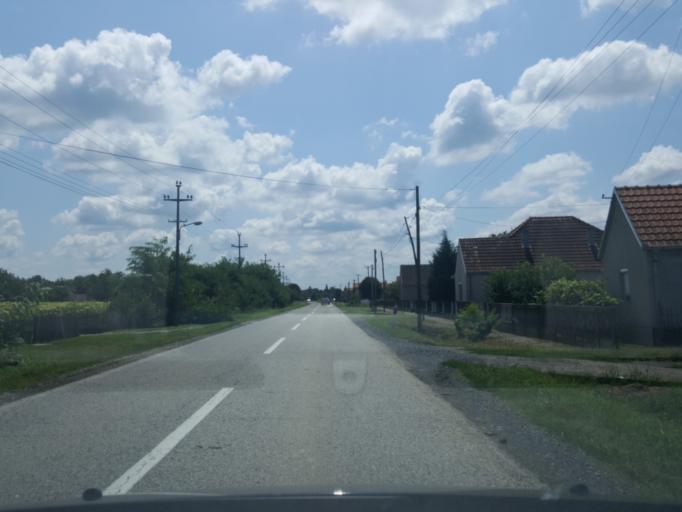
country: RS
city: Metkovic
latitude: 44.8616
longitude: 19.5446
